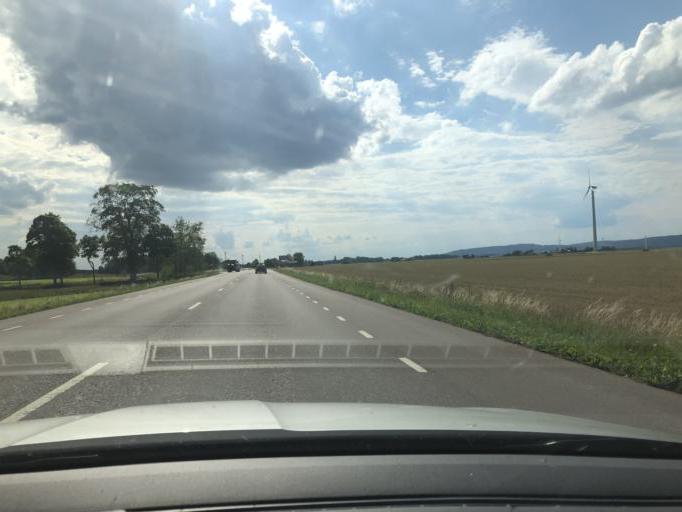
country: SE
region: OEstergoetland
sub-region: Vadstena Kommun
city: Herrestad
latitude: 58.3000
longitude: 14.8109
